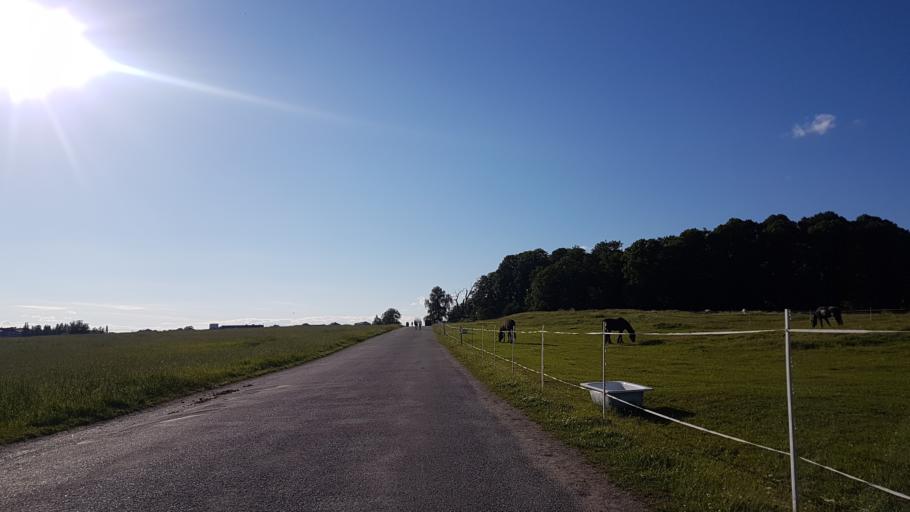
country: SE
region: Stockholm
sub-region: Stockholms Kommun
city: OEstermalm
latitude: 59.3362
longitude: 18.1184
